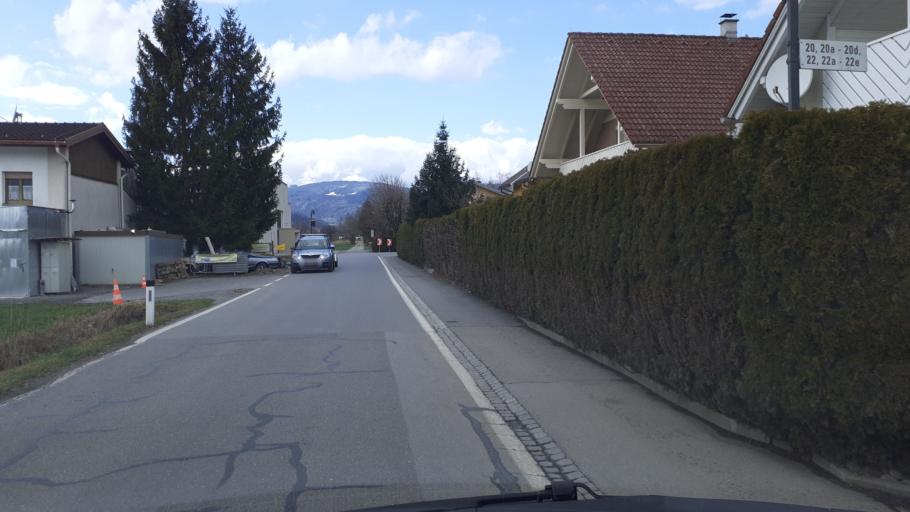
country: AT
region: Vorarlberg
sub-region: Politischer Bezirk Feldkirch
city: Koblach
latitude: 47.3164
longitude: 9.6163
